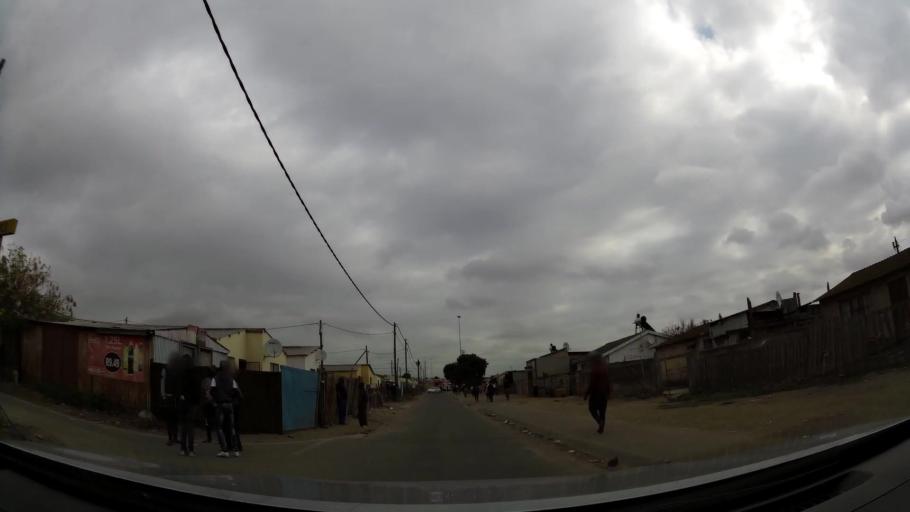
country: ZA
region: Eastern Cape
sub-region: Nelson Mandela Bay Metropolitan Municipality
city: Port Elizabeth
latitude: -33.8889
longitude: 25.5968
